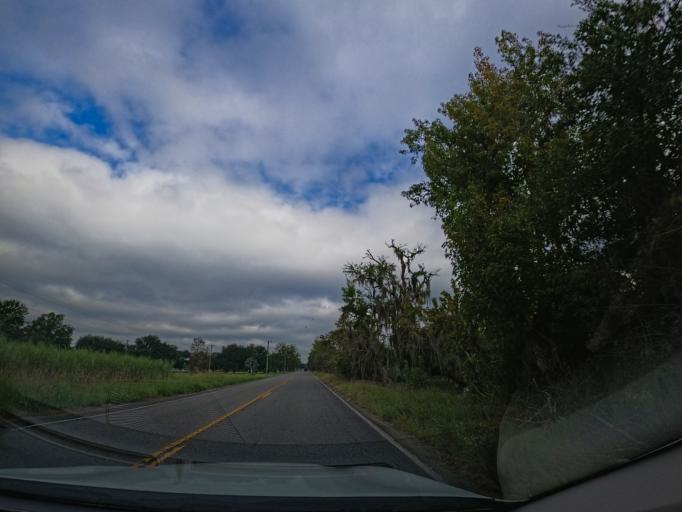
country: US
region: Louisiana
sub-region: Saint Mary Parish
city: Amelia
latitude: 29.6507
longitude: -90.9694
